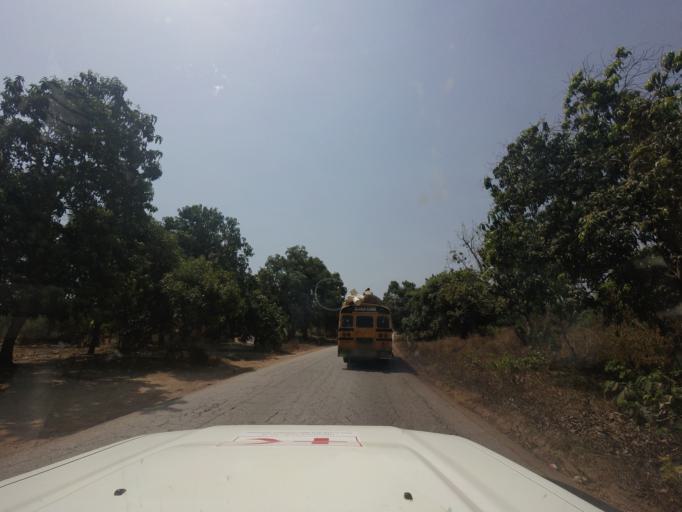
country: GN
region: Kindia
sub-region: Kindia
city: Kindia
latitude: 9.9152
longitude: -12.9966
